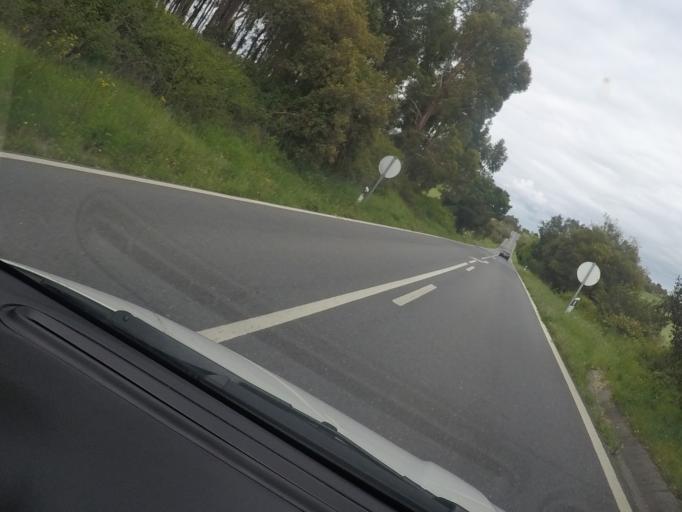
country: PT
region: Setubal
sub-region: Santiago do Cacem
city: Cercal
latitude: 37.7898
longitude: -8.6967
